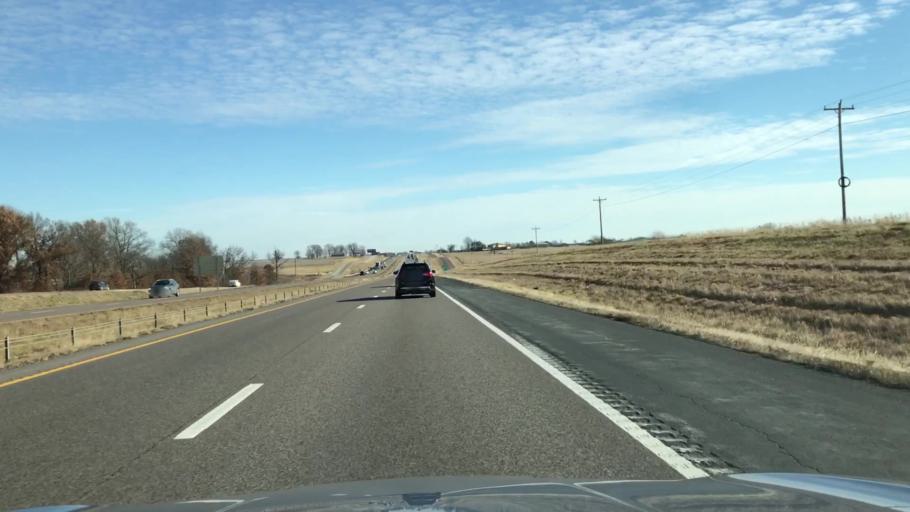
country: US
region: Missouri
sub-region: Callaway County
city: Fulton
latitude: 38.9439
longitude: -91.9141
